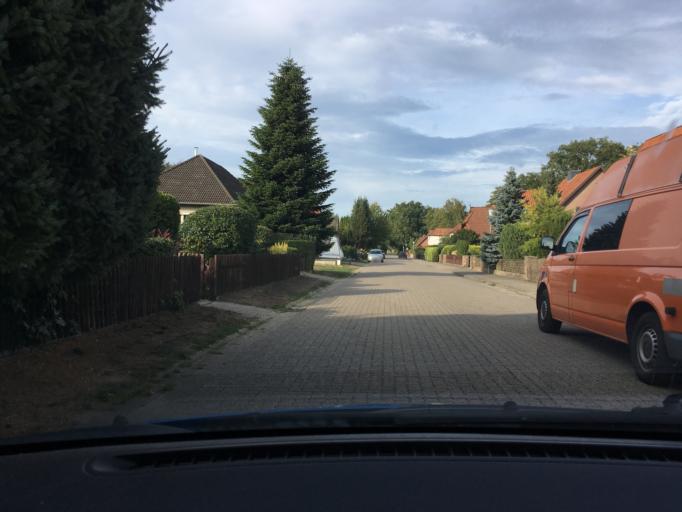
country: DE
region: Lower Saxony
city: Fassberg
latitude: 52.8803
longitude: 10.1187
